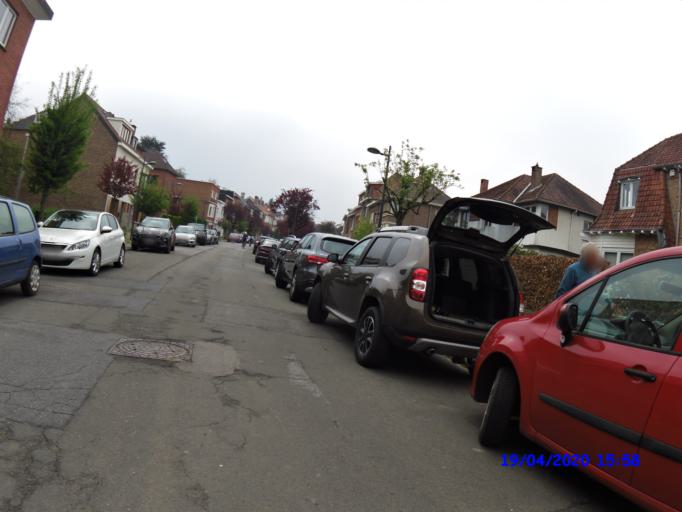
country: BE
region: Flanders
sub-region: Provincie Vlaams-Brabant
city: Kraainem
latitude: 50.8219
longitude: 4.4192
